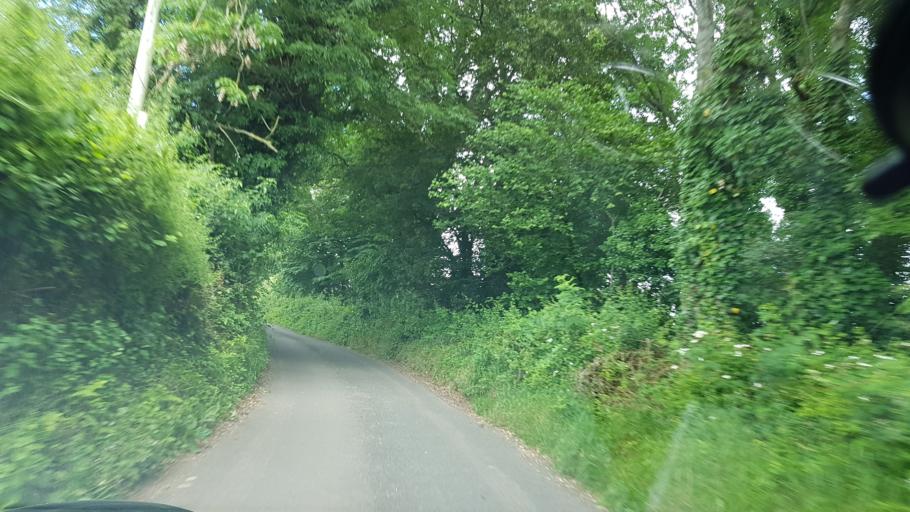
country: GB
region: Wales
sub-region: Monmouthshire
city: Llanarth
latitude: 51.8351
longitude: -2.8829
